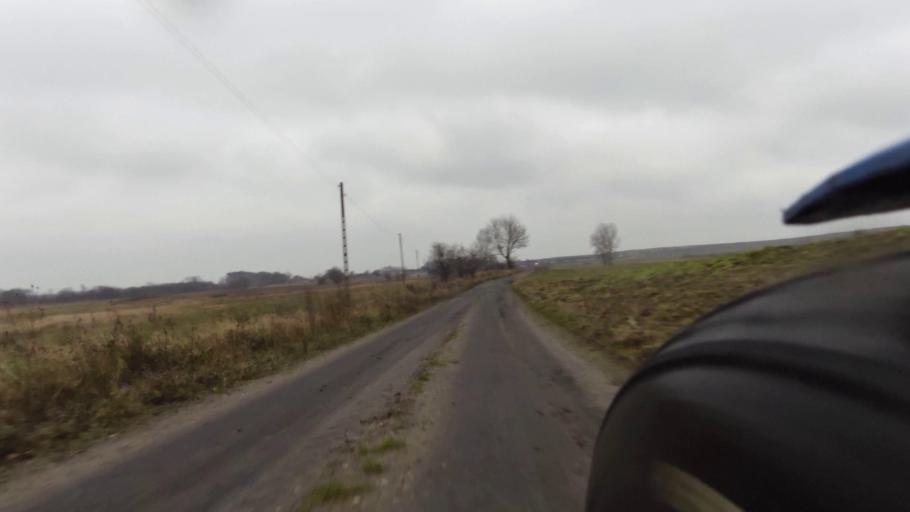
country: PL
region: West Pomeranian Voivodeship
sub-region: Powiat szczecinecki
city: Szczecinek
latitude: 53.6675
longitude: 16.6606
